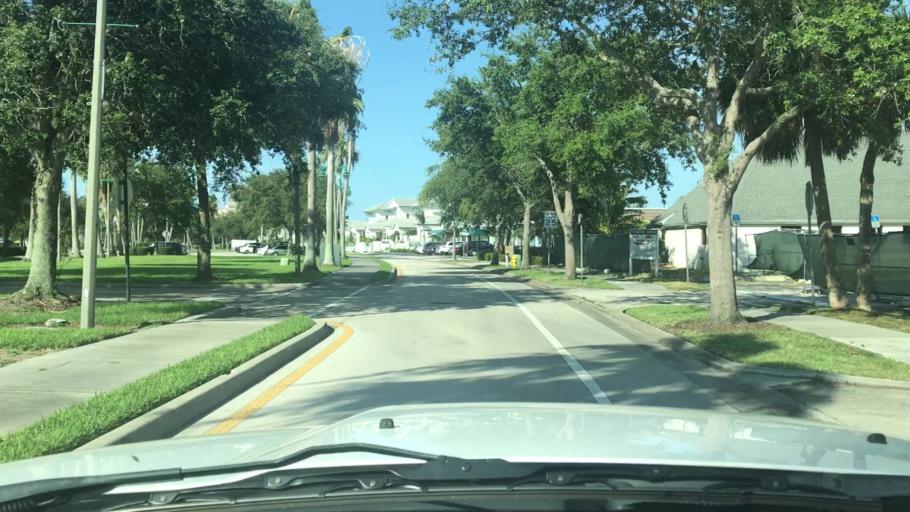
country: US
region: Florida
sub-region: Indian River County
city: Vero Beach
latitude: 27.6470
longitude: -80.3787
